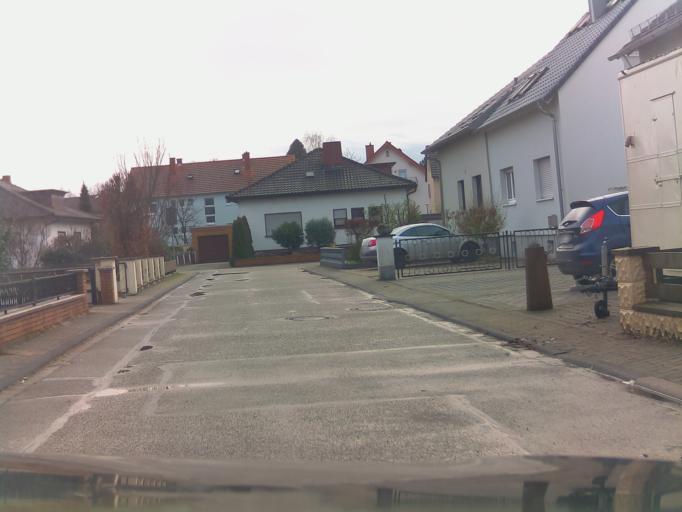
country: DE
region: Baden-Wuerttemberg
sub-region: Karlsruhe Region
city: Philippsburg
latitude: 49.2299
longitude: 8.4122
